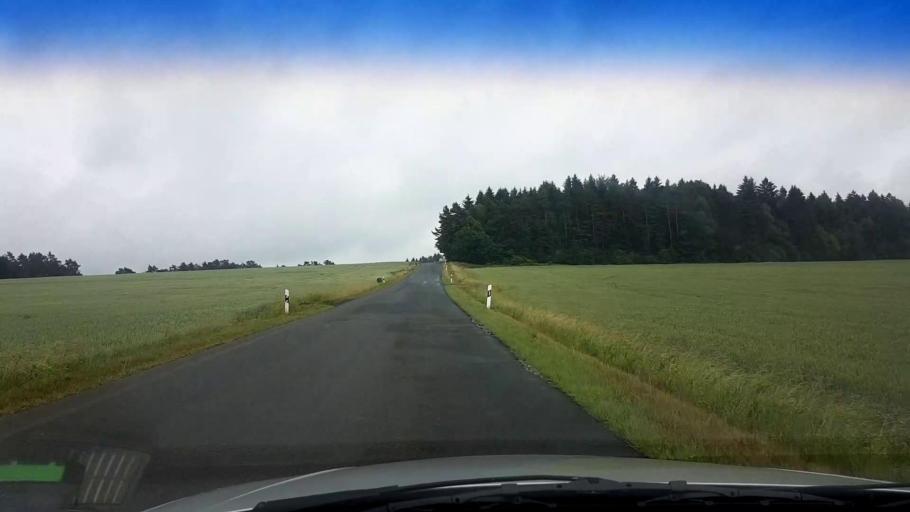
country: DE
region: Bavaria
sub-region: Upper Franconia
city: Wattendorf
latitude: 50.0540
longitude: 11.1224
